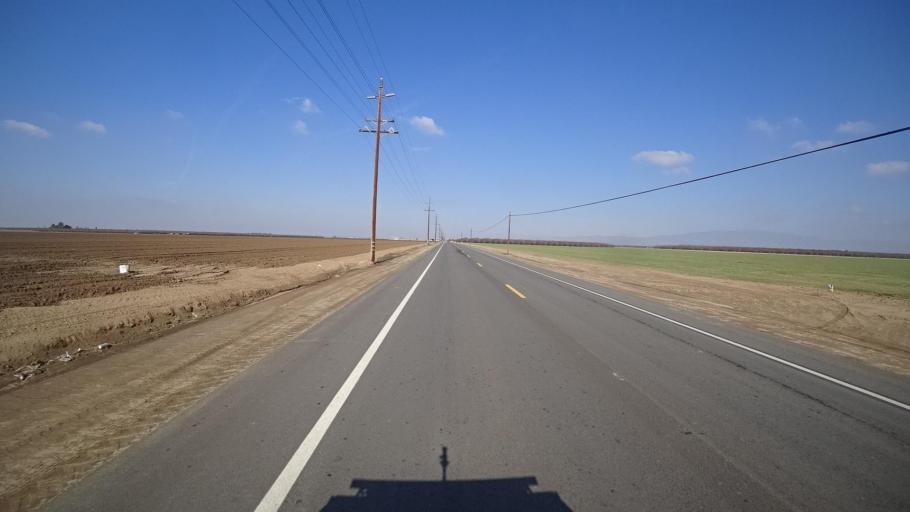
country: US
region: California
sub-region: Kern County
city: Weedpatch
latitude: 35.2126
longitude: -118.8783
